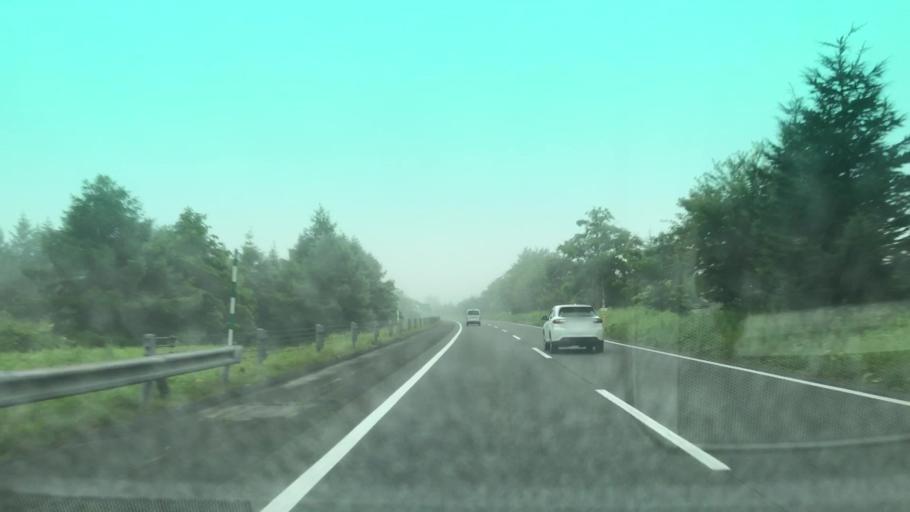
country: JP
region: Hokkaido
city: Chitose
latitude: 42.7851
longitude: 141.6264
